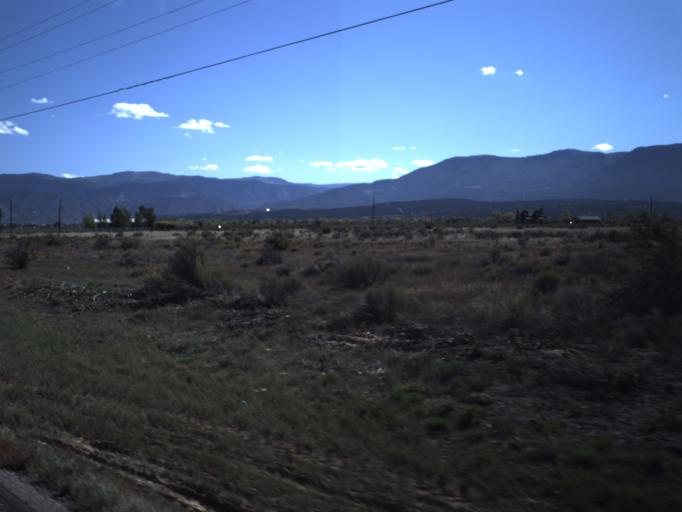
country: US
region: Utah
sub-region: Iron County
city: Cedar City
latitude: 37.6724
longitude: -113.1879
